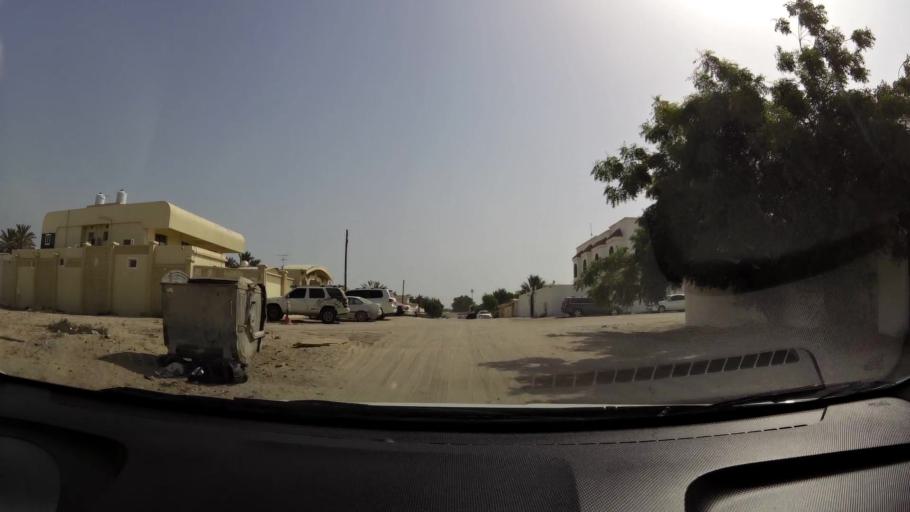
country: AE
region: Ash Shariqah
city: Sharjah
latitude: 25.3443
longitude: 55.4177
